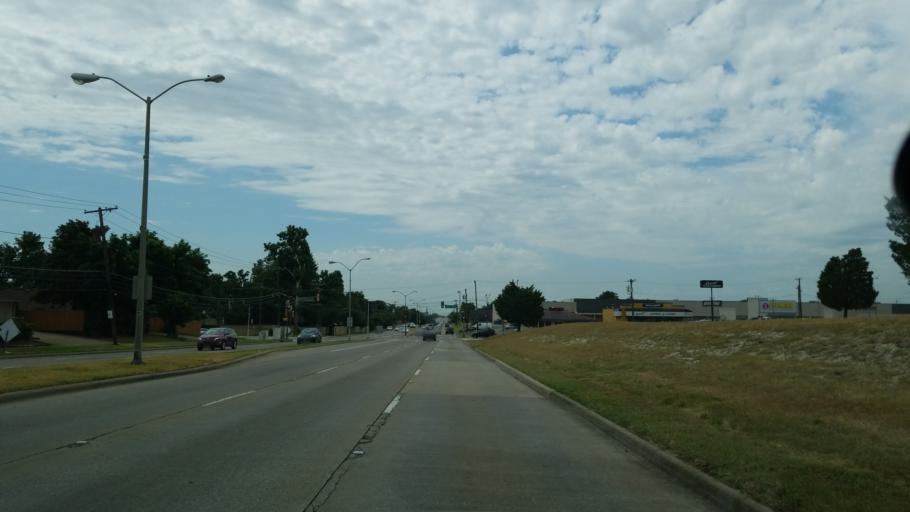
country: US
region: Texas
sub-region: Dallas County
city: Duncanville
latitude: 32.6728
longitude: -96.8572
